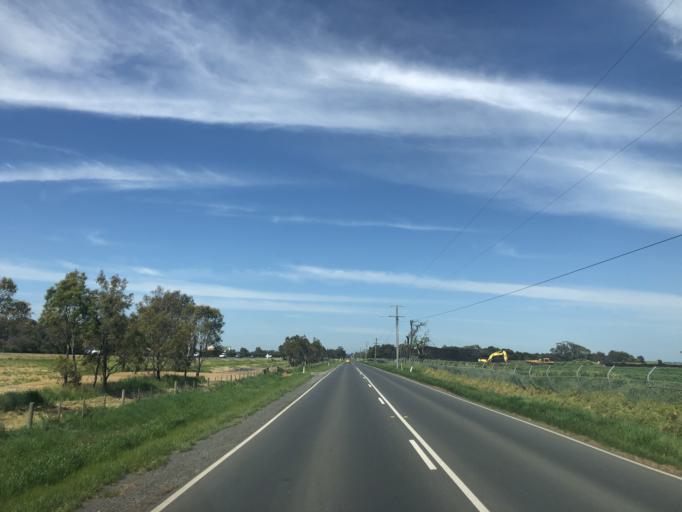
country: AU
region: Victoria
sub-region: Frankston
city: Sandhurst
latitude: -38.0432
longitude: 145.1863
